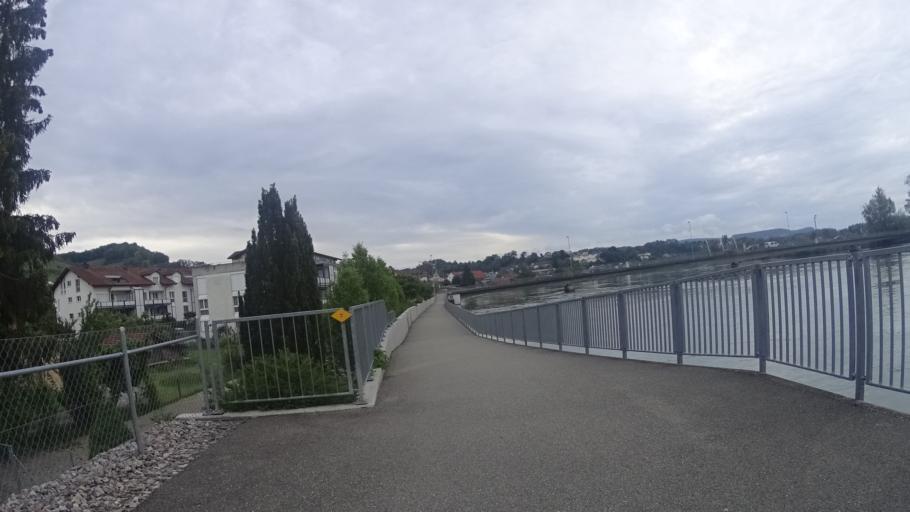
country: CH
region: Aargau
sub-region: Bezirk Zurzach
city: Klingnau
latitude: 47.5749
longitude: 8.2521
